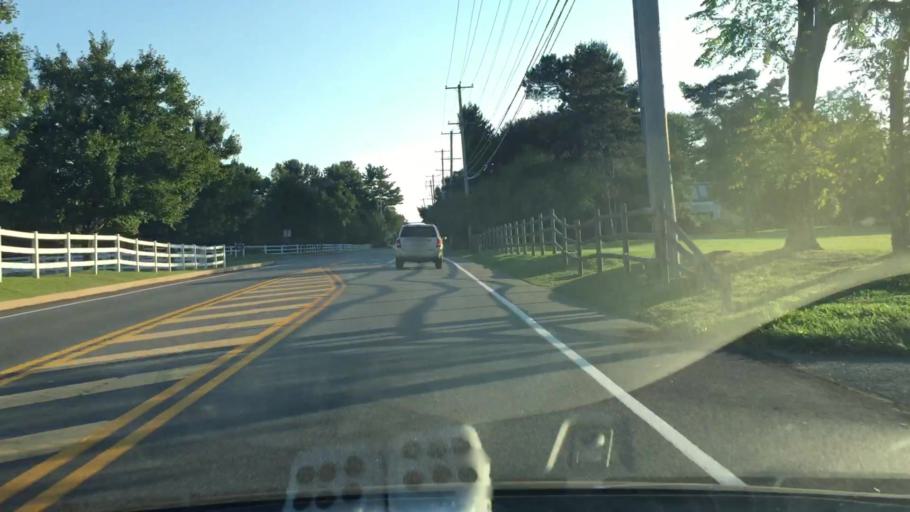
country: US
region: Pennsylvania
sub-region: Delaware County
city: Chester Heights
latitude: 39.8468
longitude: -75.4879
